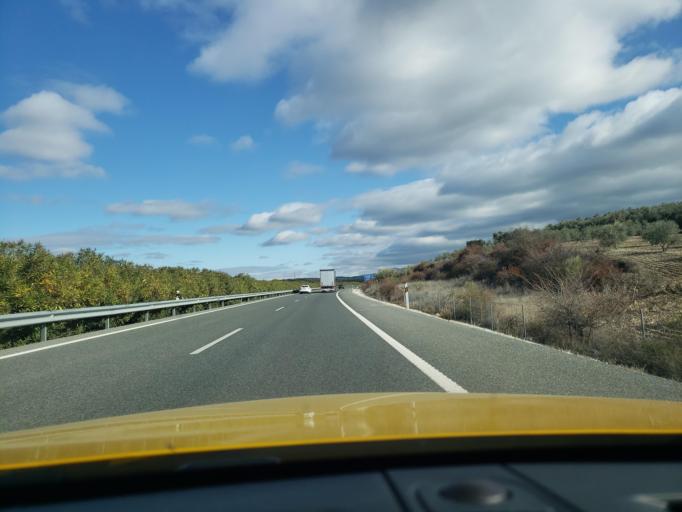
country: ES
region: Andalusia
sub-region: Provincia de Malaga
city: Villanueva del Trabuco
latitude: 37.0631
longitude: -4.3445
